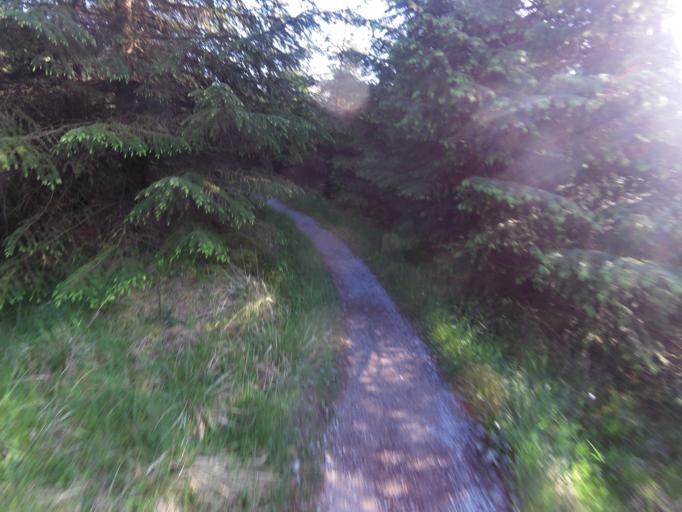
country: GB
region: England
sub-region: North Yorkshire
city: Settle
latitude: 54.0219
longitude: -2.3850
